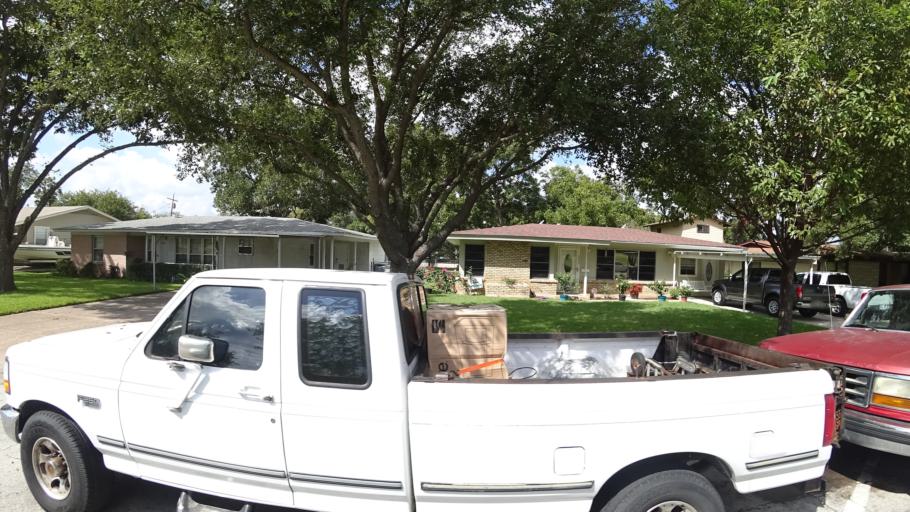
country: US
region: Texas
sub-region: Travis County
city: Austin
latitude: 30.3543
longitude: -97.7216
